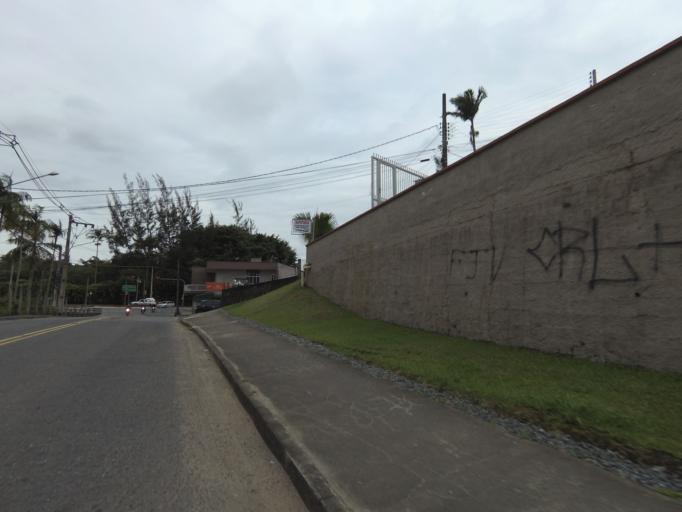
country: BR
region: Santa Catarina
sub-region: Blumenau
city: Blumenau
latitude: -26.8941
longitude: -49.1279
